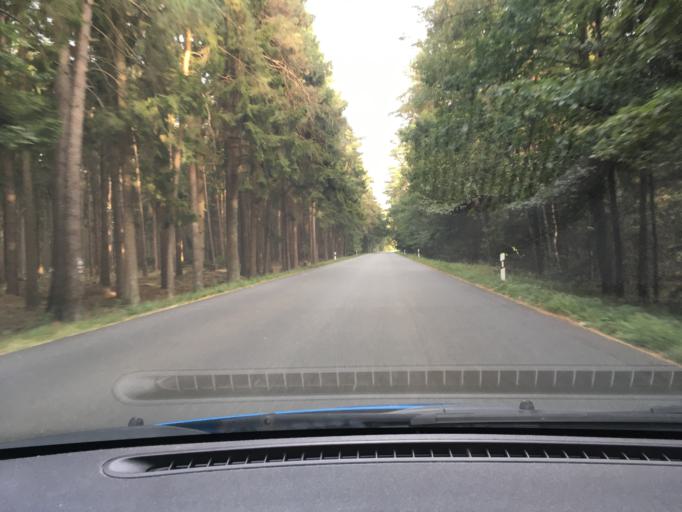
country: DE
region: Lower Saxony
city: Wietzendorf
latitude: 52.9667
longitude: 9.9503
